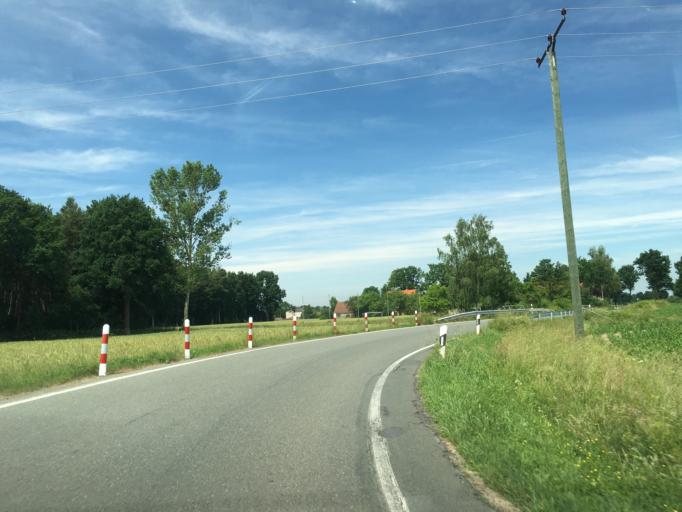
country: DE
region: North Rhine-Westphalia
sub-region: Regierungsbezirk Munster
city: Nordwalde
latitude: 52.1388
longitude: 7.4305
